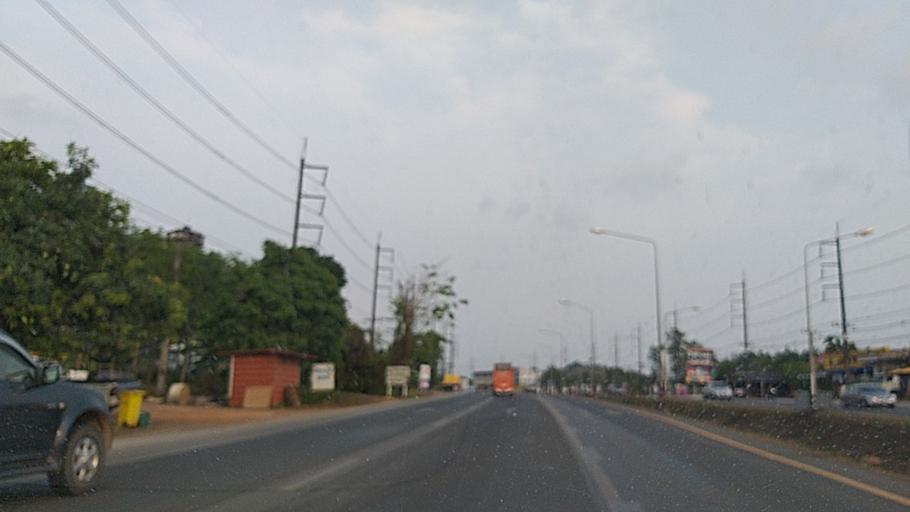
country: TH
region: Trat
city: Khao Saming
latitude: 12.3676
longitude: 102.3939
